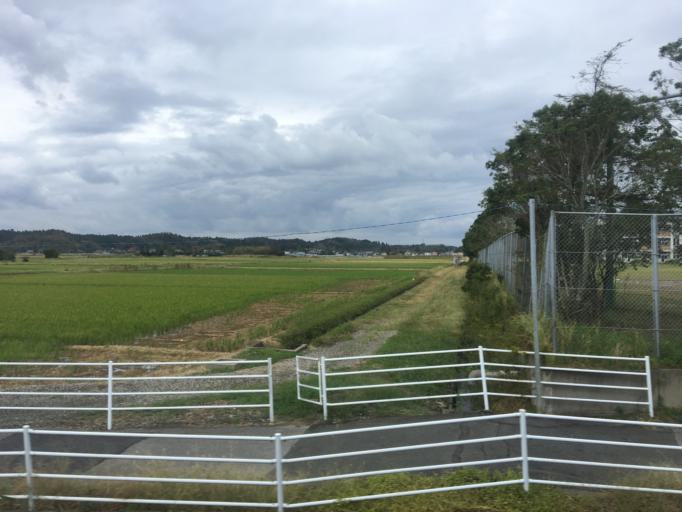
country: JP
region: Chiba
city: Togane
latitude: 35.5495
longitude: 140.3456
